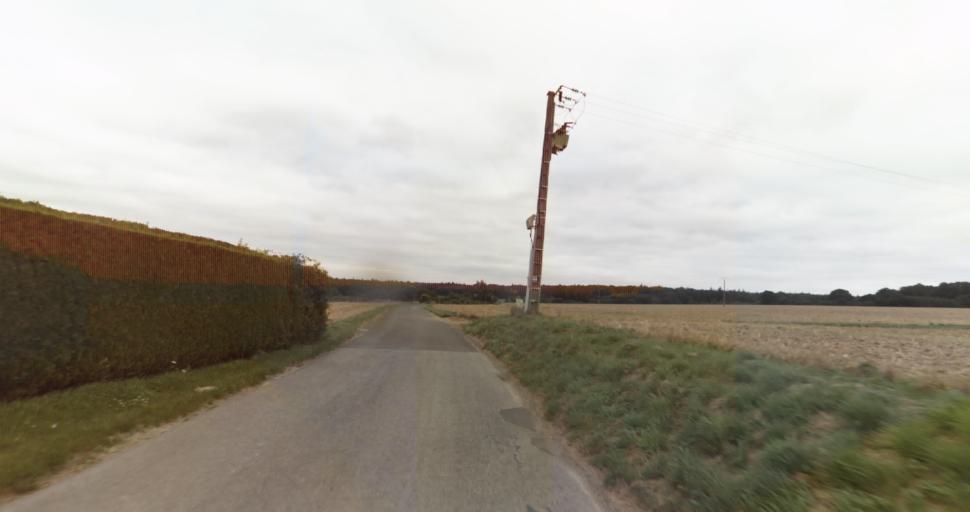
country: FR
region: Haute-Normandie
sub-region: Departement de l'Eure
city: Marcilly-sur-Eure
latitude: 48.8831
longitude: 1.3091
